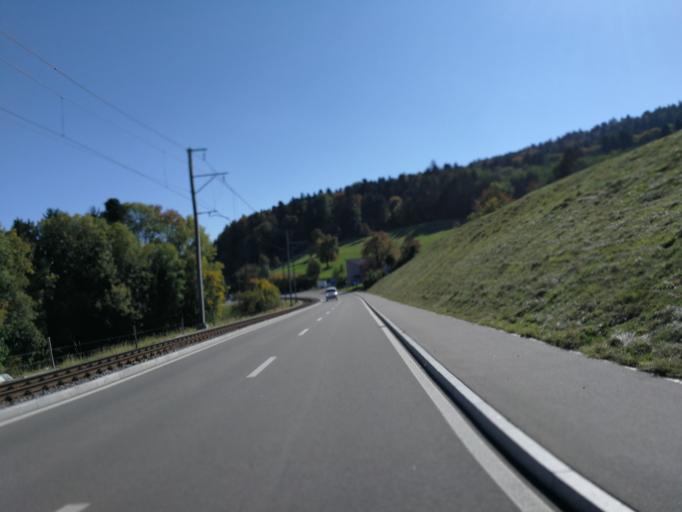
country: CH
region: Zurich
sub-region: Bezirk Uster
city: Aesch
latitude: 47.3182
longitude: 8.6656
